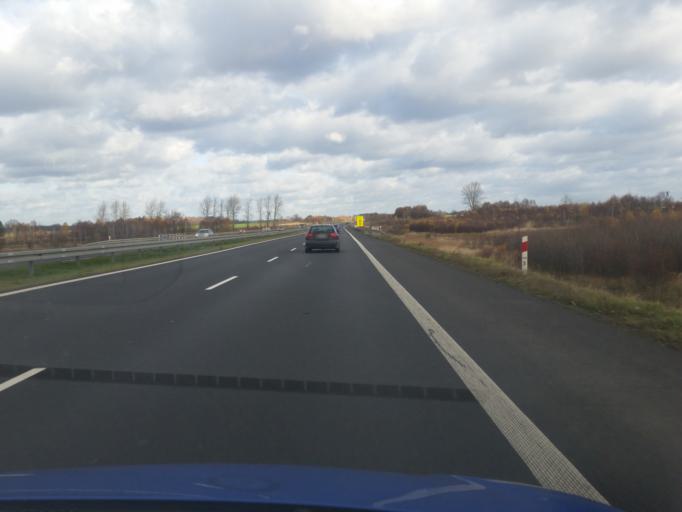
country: PL
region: Silesian Voivodeship
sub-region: Powiat czestochowski
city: Mykanow
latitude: 50.9381
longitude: 19.2342
